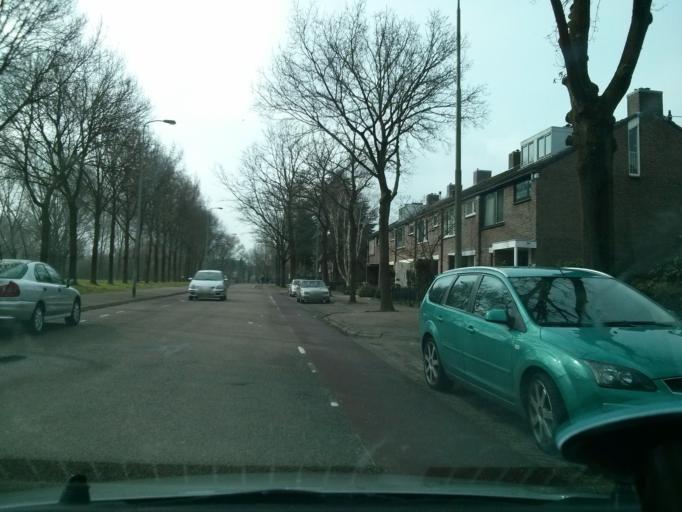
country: NL
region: North Brabant
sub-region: Gemeente Son en Breugel
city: Son
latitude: 51.4850
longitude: 5.5048
